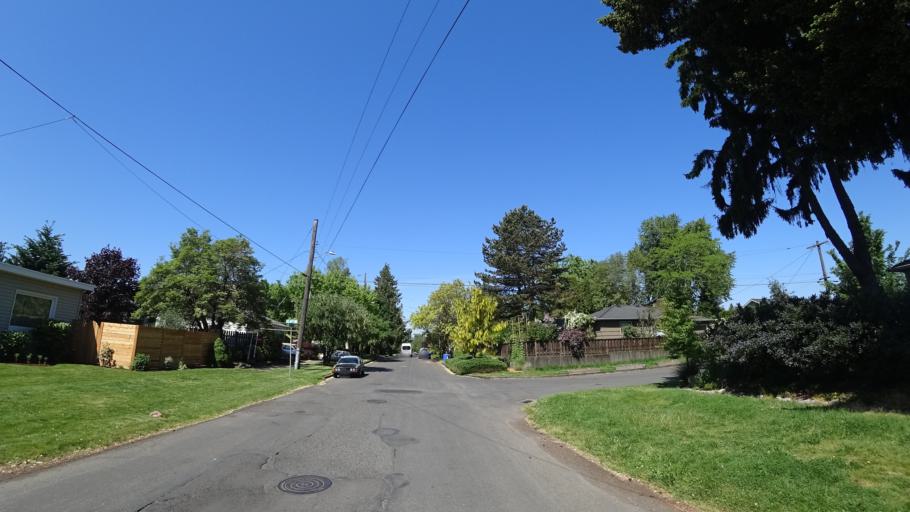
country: US
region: Oregon
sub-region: Multnomah County
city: Lents
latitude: 45.4867
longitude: -122.6137
